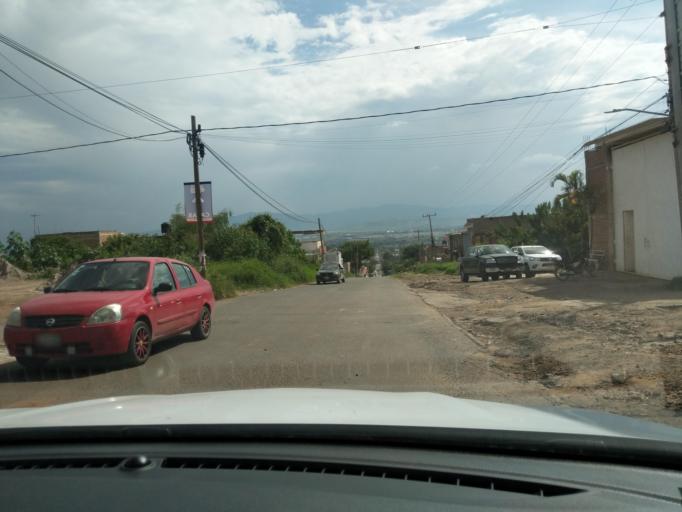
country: MX
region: Jalisco
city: San Jose del Castillo
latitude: 20.5230
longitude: -103.2338
